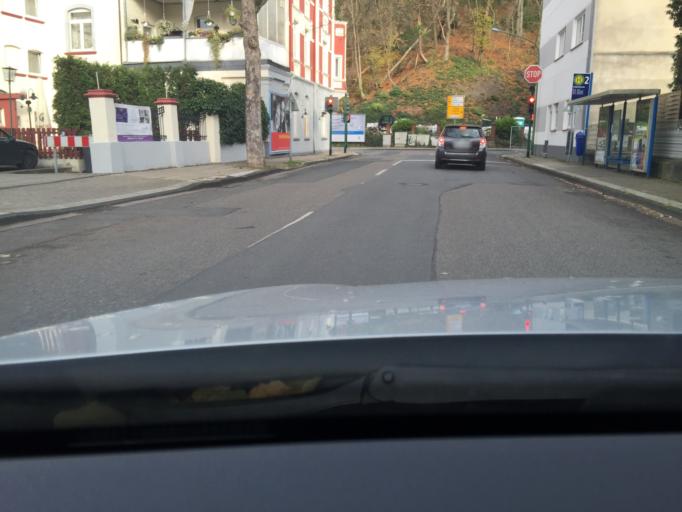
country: DE
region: North Rhine-Westphalia
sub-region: Regierungsbezirk Dusseldorf
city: Velbert
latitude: 51.3857
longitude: 7.0852
